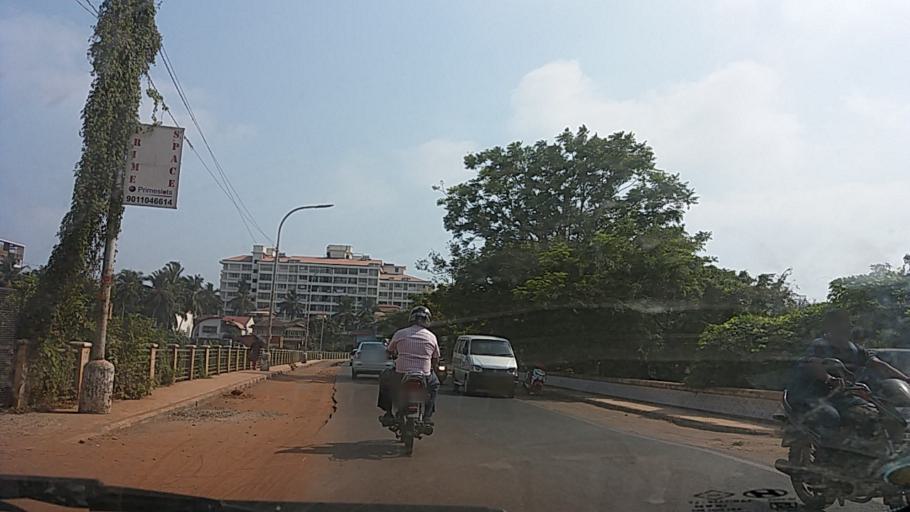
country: IN
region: Goa
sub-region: North Goa
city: Panaji
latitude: 15.4791
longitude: 73.8123
